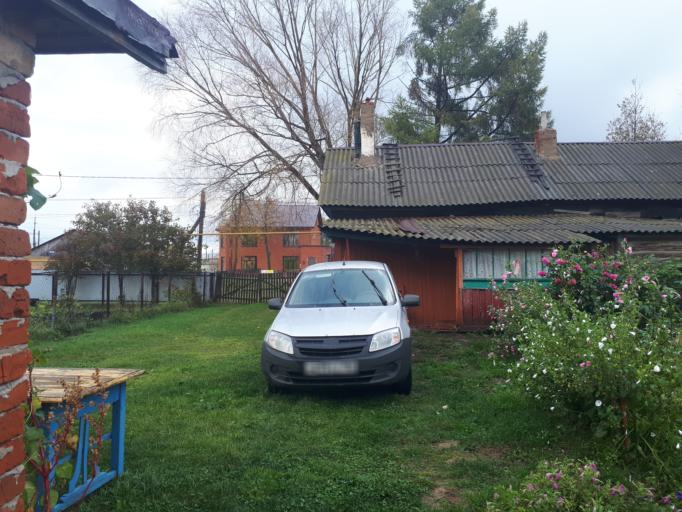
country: RU
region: Bashkortostan
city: Tolbazy
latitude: 53.9877
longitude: 55.9077
